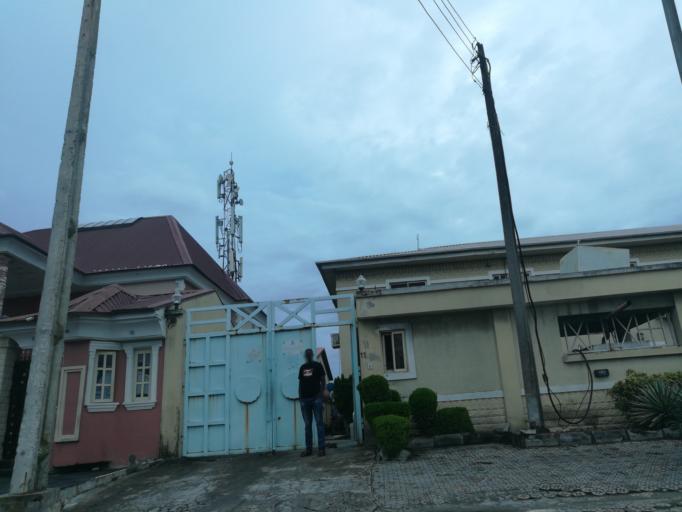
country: NG
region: Lagos
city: Ikoyi
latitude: 6.4418
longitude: 3.4746
